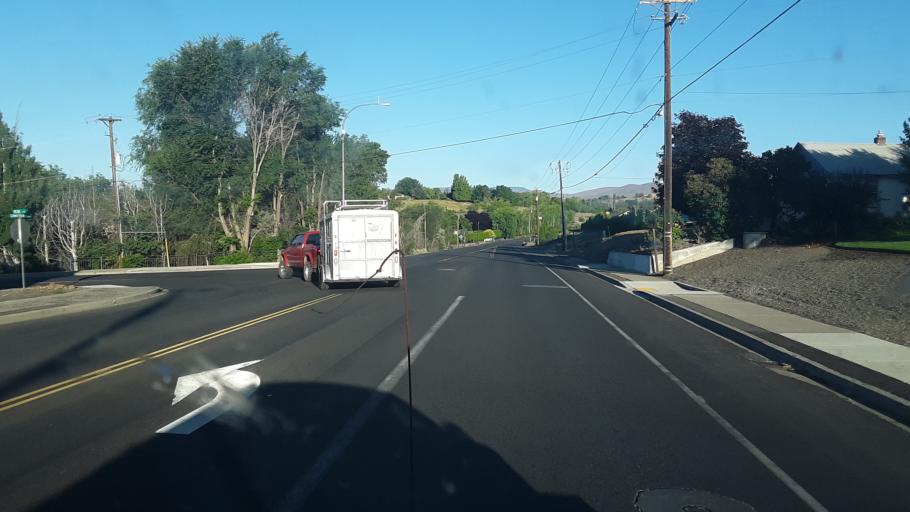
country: US
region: Washington
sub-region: Yakima County
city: West Valley
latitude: 46.6003
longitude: -120.6405
